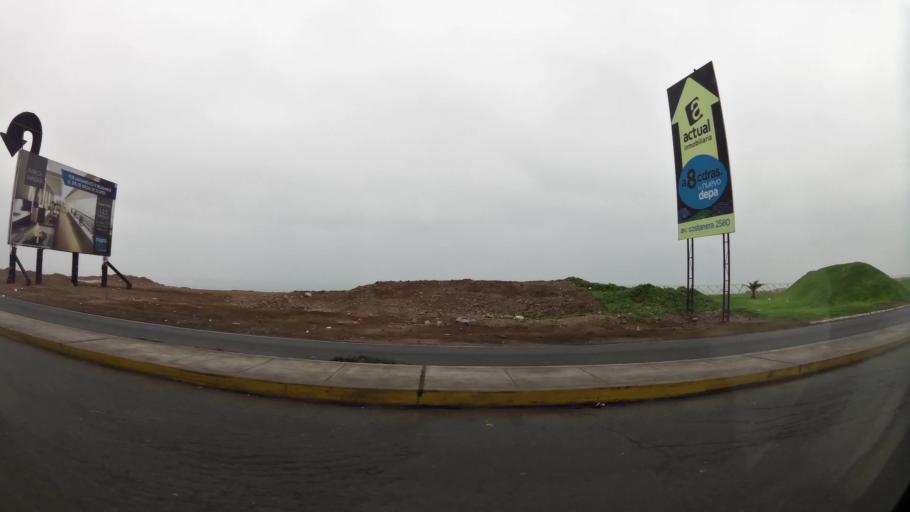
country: PE
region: Callao
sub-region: Callao
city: Callao
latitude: -12.0861
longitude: -77.0963
